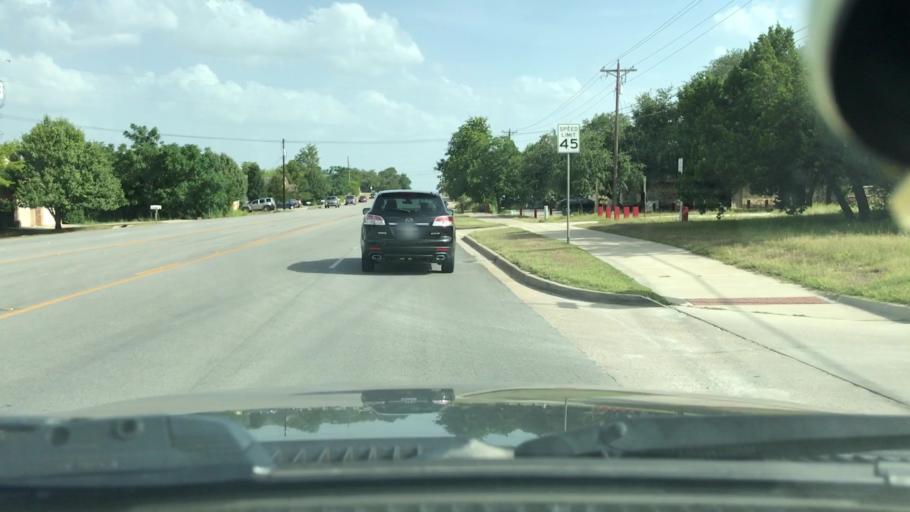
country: US
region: Texas
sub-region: Williamson County
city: Leander
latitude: 30.5465
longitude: -97.8520
